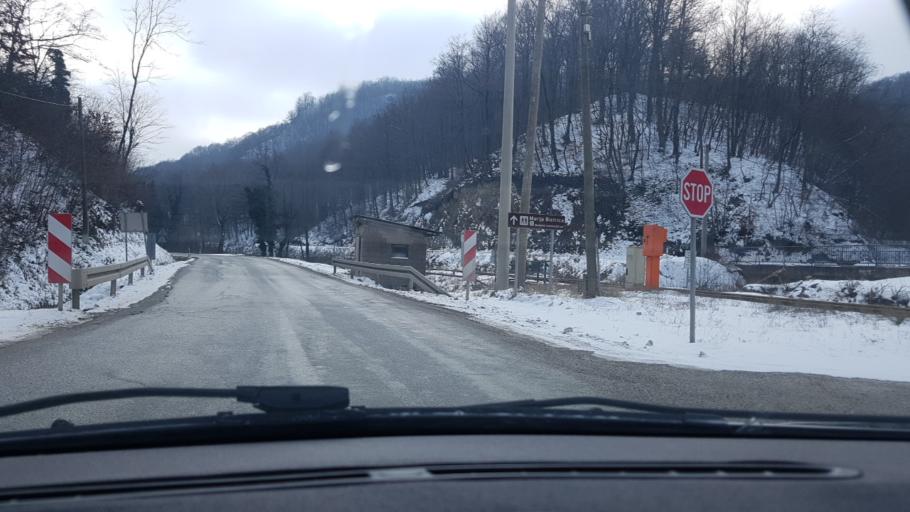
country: HR
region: Krapinsko-Zagorska
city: Mihovljan
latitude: 46.1855
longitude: 15.9843
